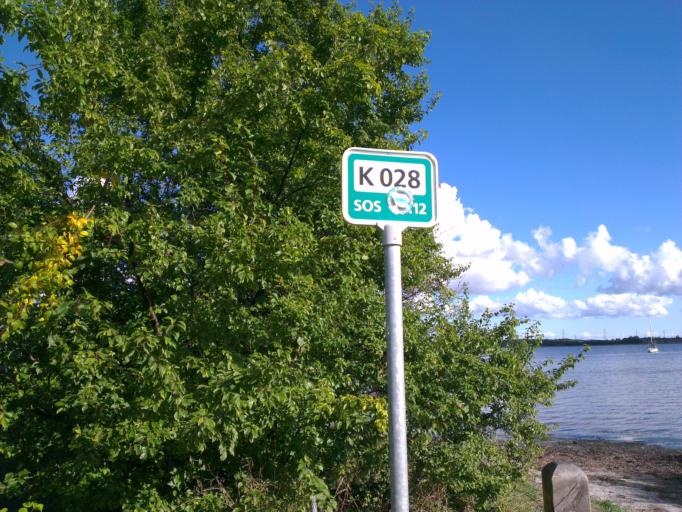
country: DK
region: Capital Region
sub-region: Frederikssund Kommune
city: Frederikssund
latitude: 55.7925
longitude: 12.0558
